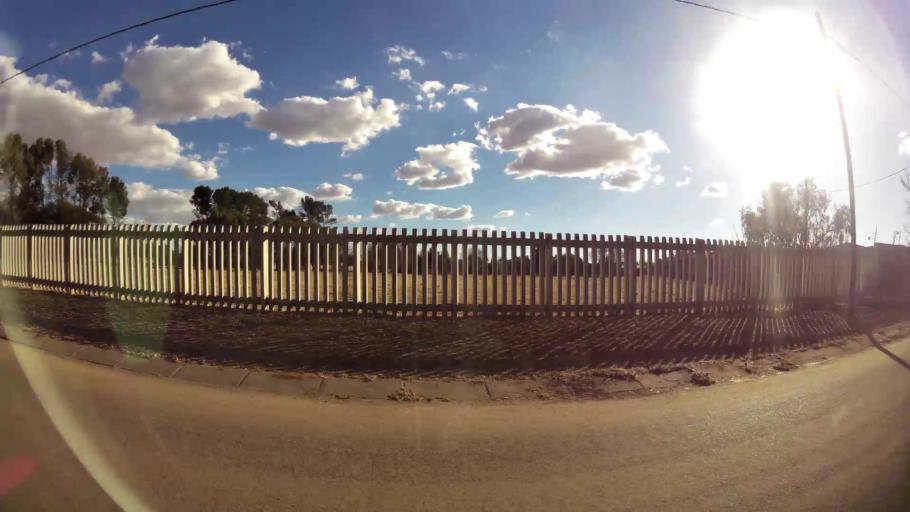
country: ZA
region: North-West
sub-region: Dr Kenneth Kaunda District Municipality
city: Klerksdorp
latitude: -26.8391
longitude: 26.6626
